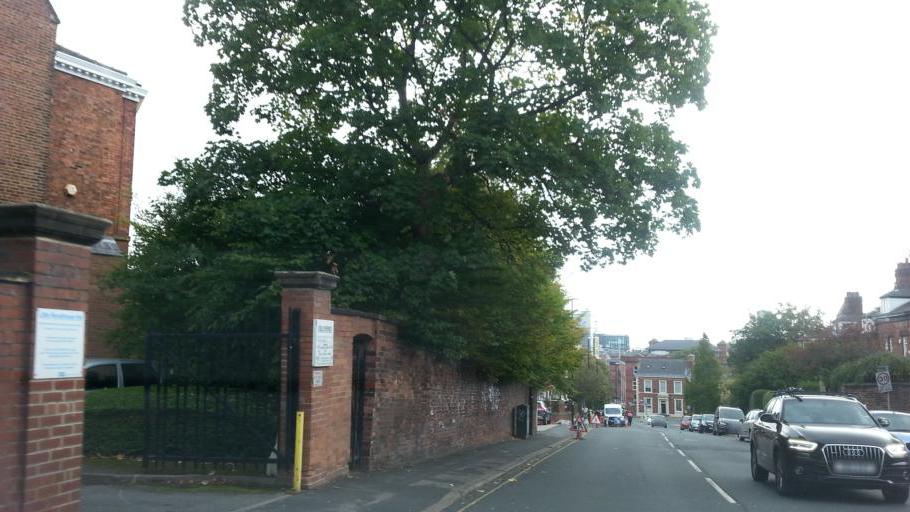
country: GB
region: England
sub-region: City and Borough of Leeds
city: Leeds
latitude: 53.8028
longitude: -1.5577
